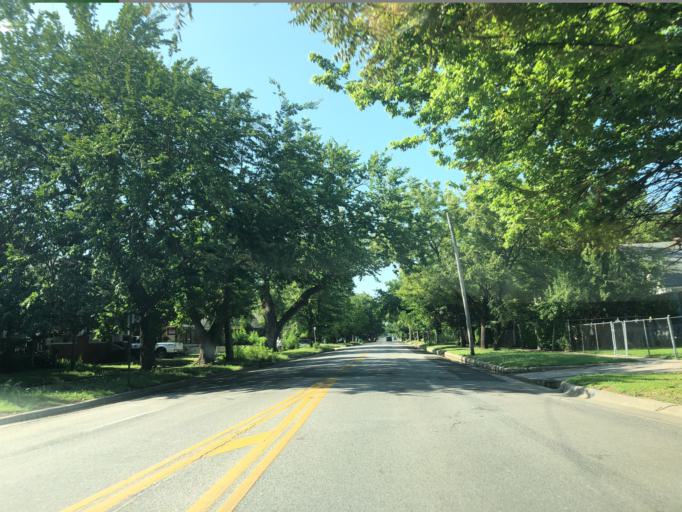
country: US
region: Kansas
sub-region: Sedgwick County
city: Wichita
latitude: 37.7073
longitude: -97.3420
